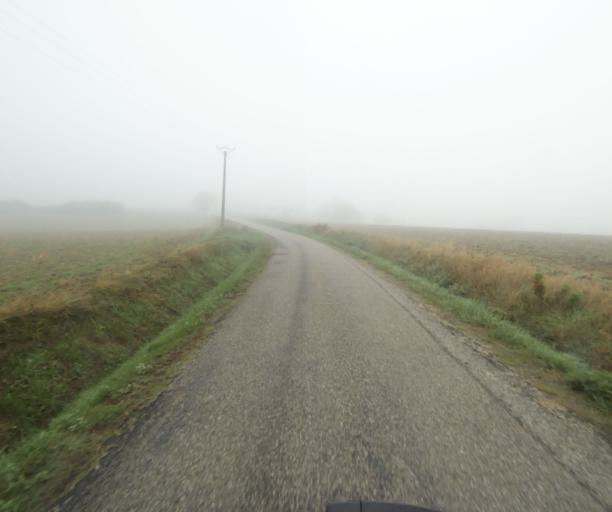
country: FR
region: Midi-Pyrenees
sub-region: Departement de la Haute-Garonne
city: Villemur-sur-Tarn
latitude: 43.9075
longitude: 1.4853
